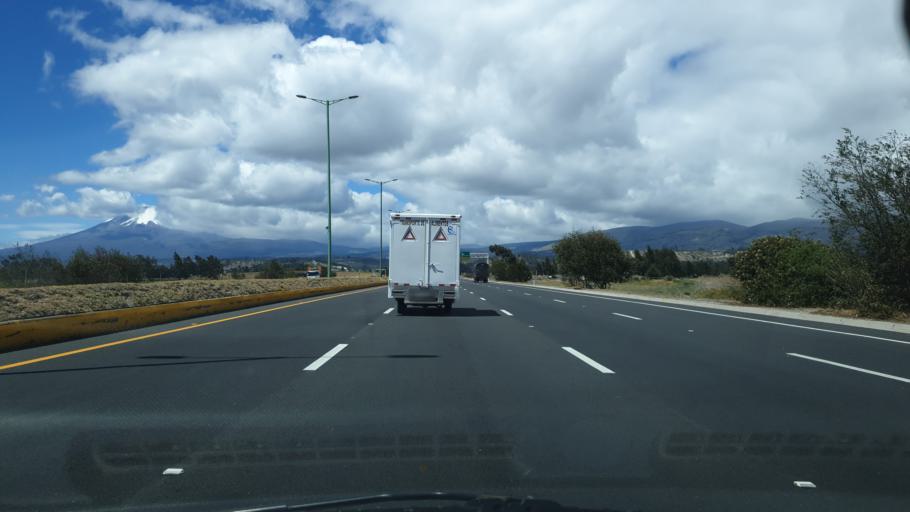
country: EC
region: Cotopaxi
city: Saquisili
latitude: -0.8695
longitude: -78.6340
